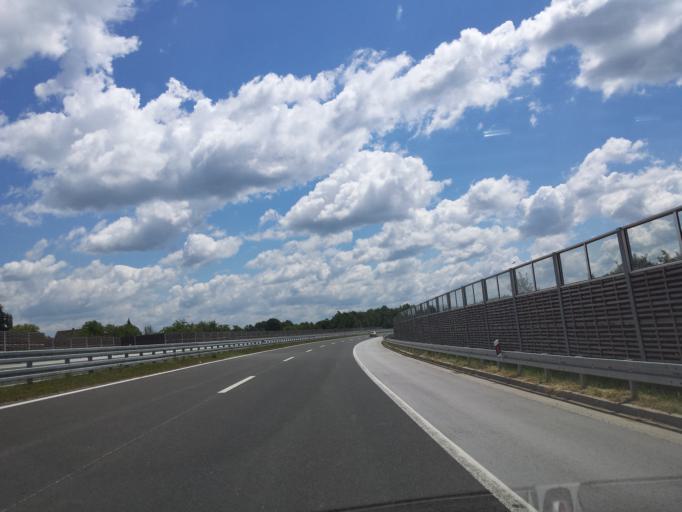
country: HR
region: Zagrebacka
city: Turopolje
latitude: 45.6021
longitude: 16.1342
